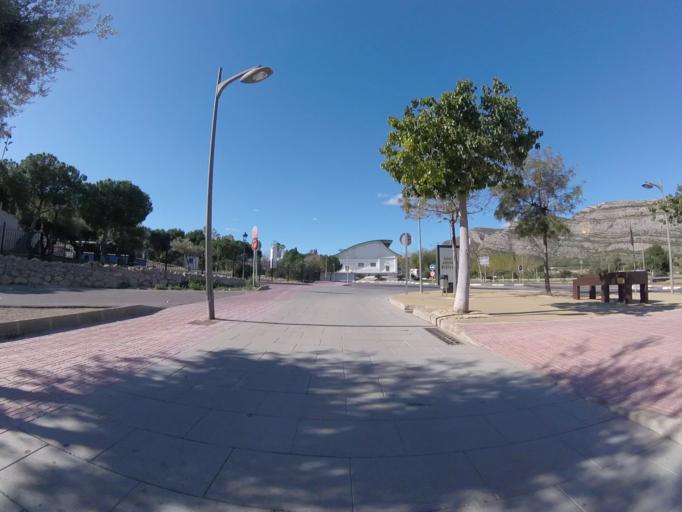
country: ES
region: Valencia
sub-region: Provincia de Castello
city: Orpesa/Oropesa del Mar
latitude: 40.0932
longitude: 0.1317
